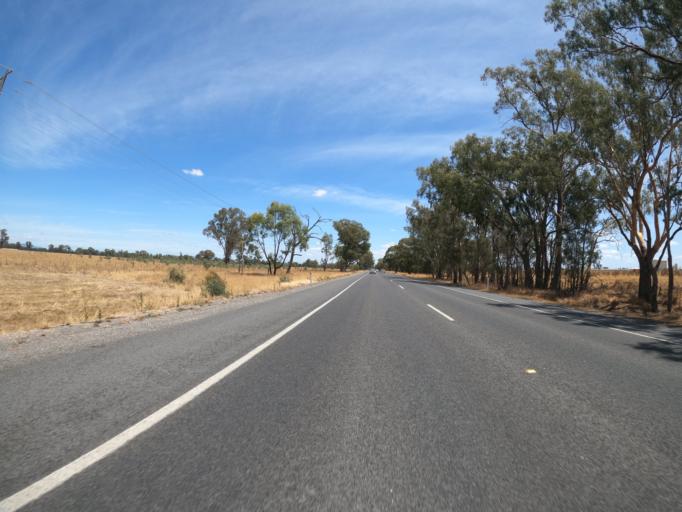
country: AU
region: Victoria
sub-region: Benalla
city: Benalla
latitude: -36.5269
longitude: 146.0489
